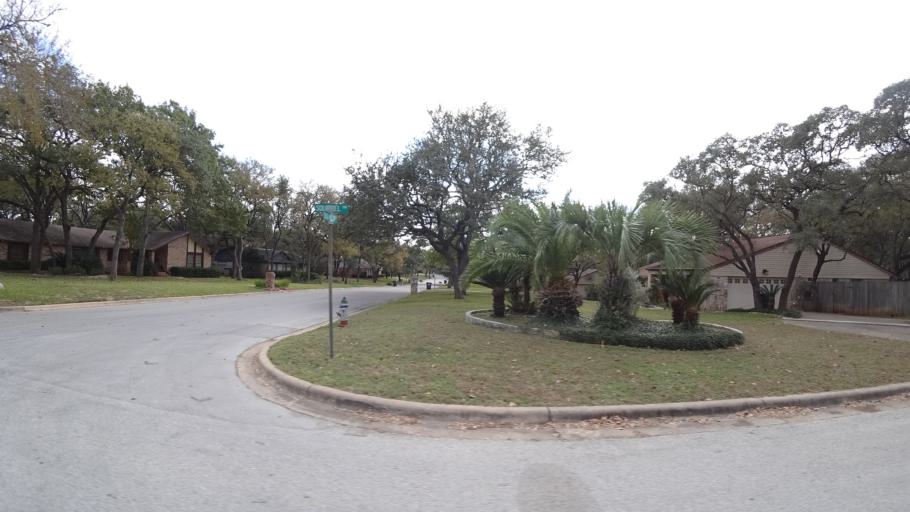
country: US
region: Texas
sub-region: Travis County
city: Shady Hollow
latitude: 30.1731
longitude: -97.8551
